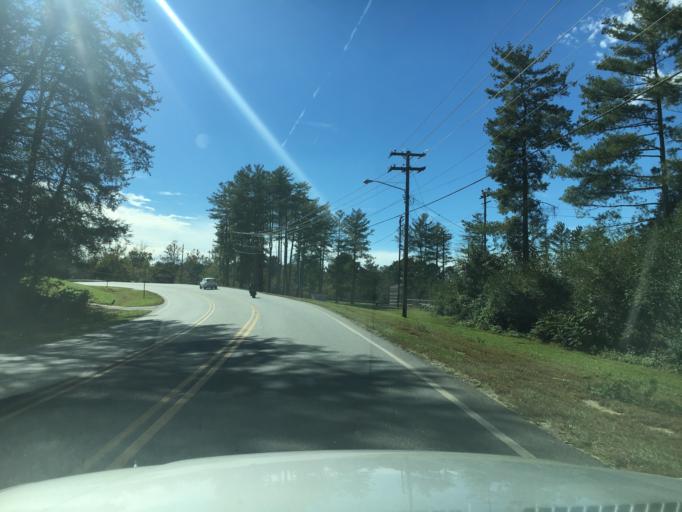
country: US
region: North Carolina
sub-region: Burke County
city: Morganton
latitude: 35.7604
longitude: -81.7015
